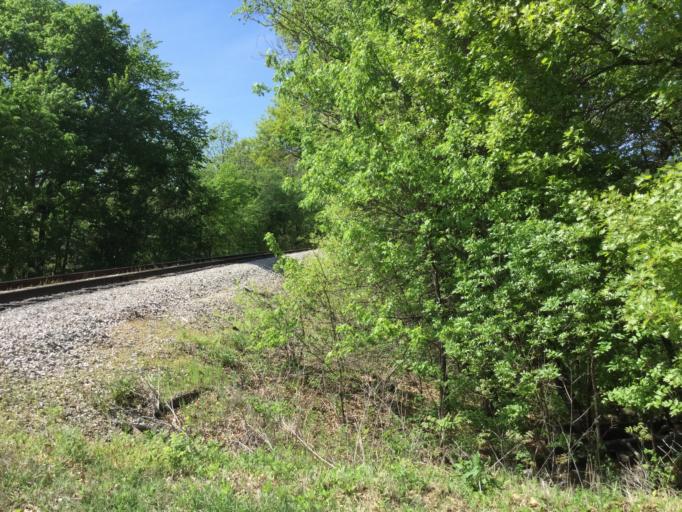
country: US
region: Kansas
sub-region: Montgomery County
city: Cherryvale
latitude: 37.2961
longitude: -95.5780
